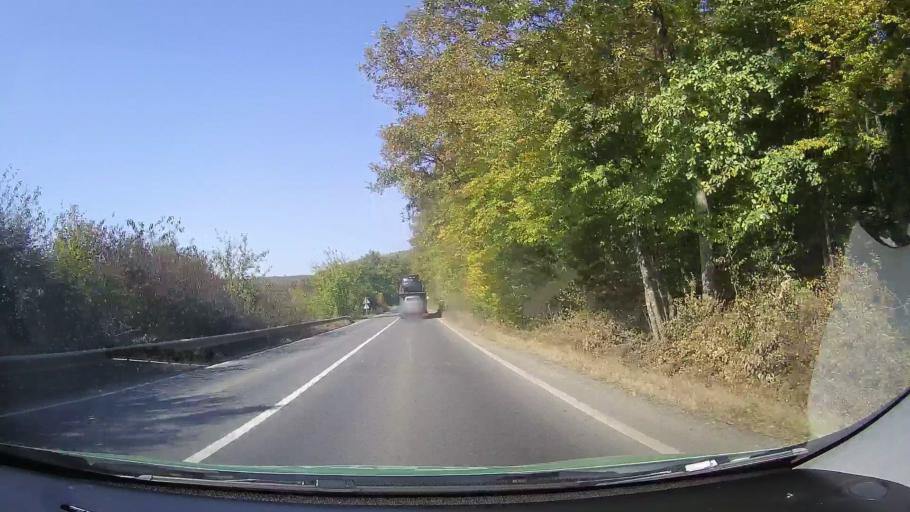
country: RO
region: Arad
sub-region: Comuna Conop
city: Conop
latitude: 46.1106
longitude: 21.8493
